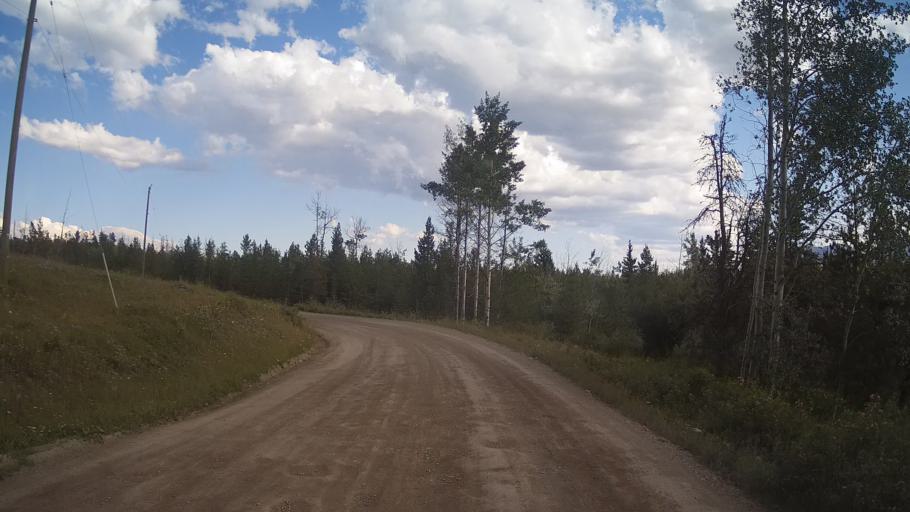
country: CA
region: British Columbia
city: Lillooet
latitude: 51.2848
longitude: -121.7472
